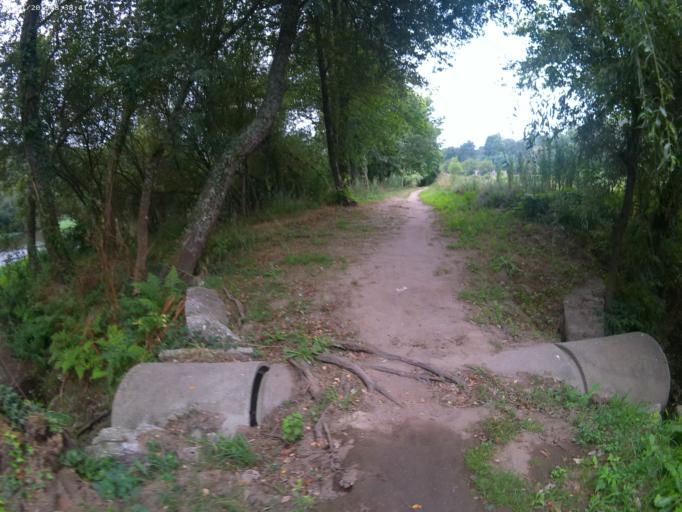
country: PT
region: Viana do Castelo
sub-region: Ponte da Barca
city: Ponte da Barca
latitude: 41.8141
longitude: -8.4280
